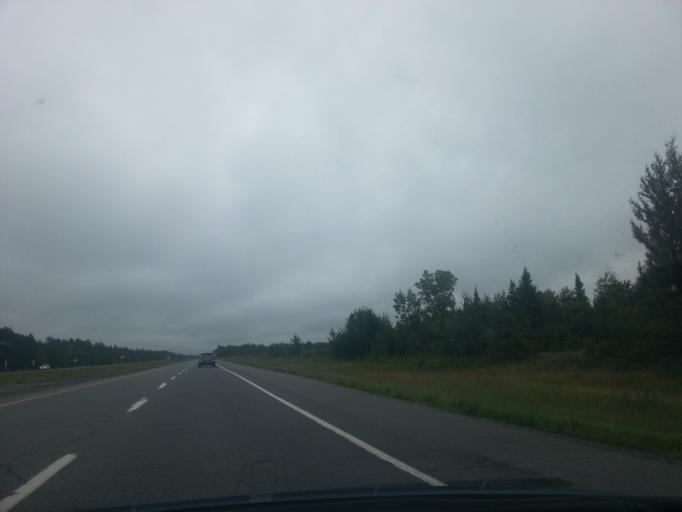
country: CA
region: Quebec
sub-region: Mauricie
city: Daveluyville
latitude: 46.2425
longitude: -72.0583
